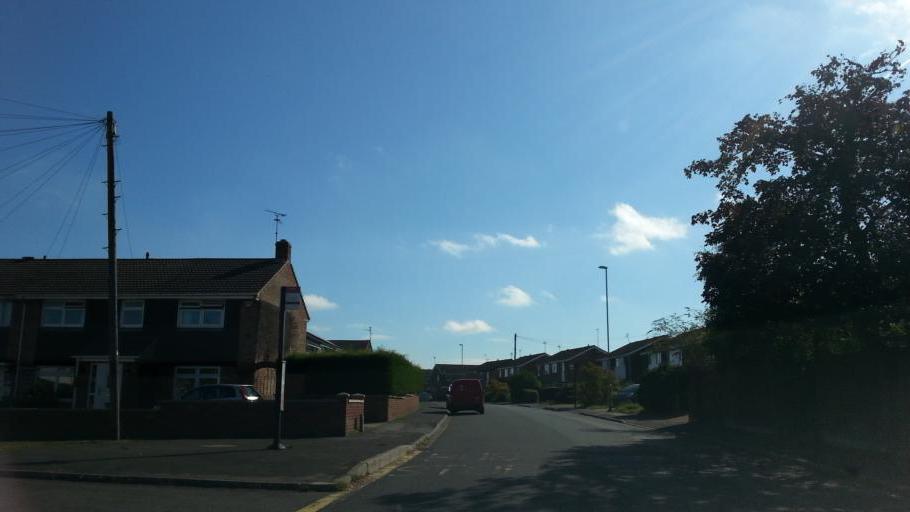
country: GB
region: England
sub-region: Northamptonshire
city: Rushden
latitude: 52.2803
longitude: -0.6072
